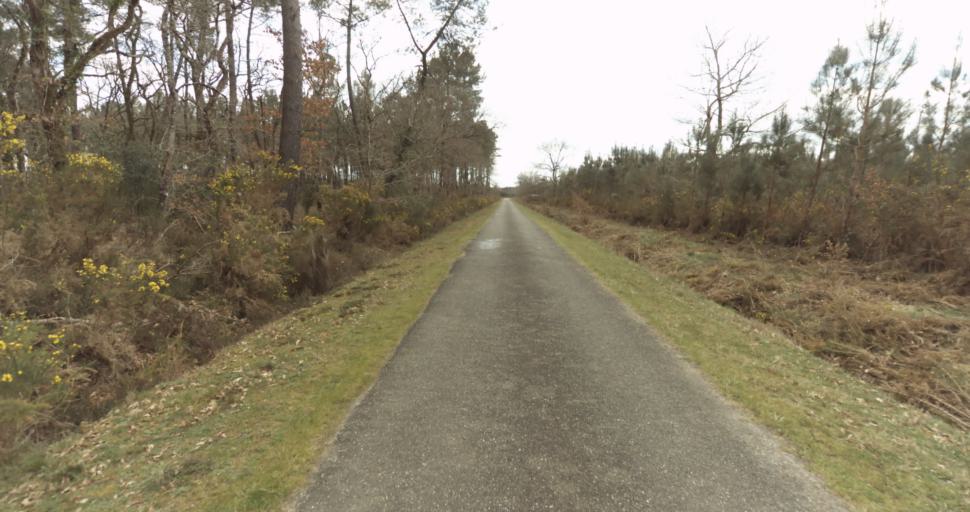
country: FR
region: Aquitaine
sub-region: Departement des Landes
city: Roquefort
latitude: 44.0825
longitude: -0.4411
